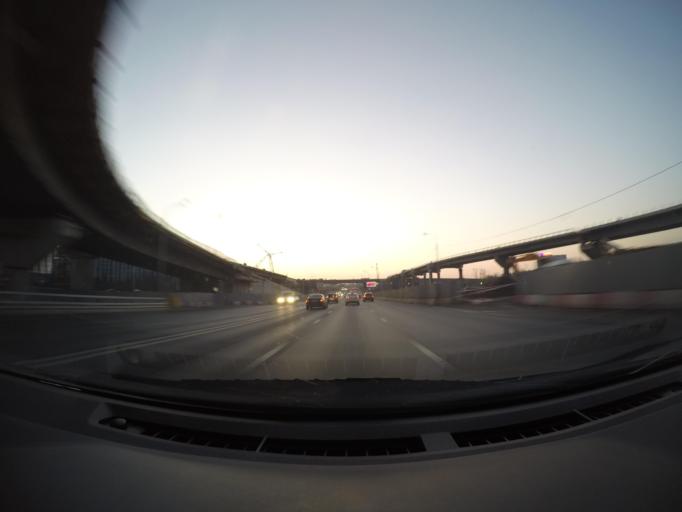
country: RU
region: Moscow
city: Tekstil'shchiki
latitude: 55.7120
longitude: 37.7219
